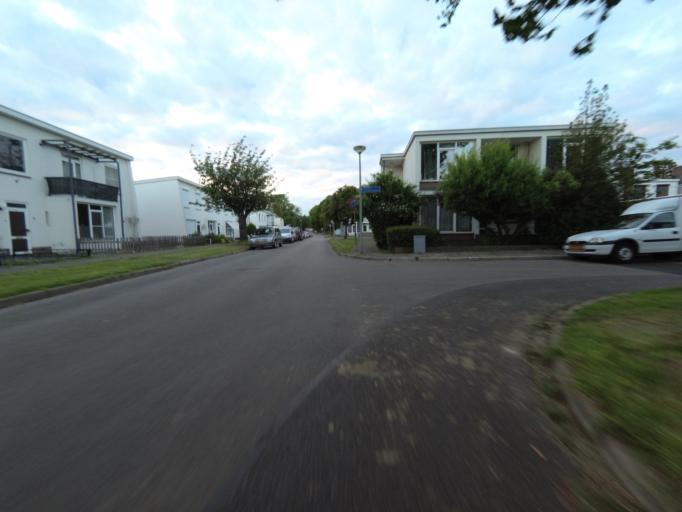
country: NL
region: Limburg
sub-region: Gemeente Maastricht
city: Heer
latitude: 50.8627
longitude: 5.7296
